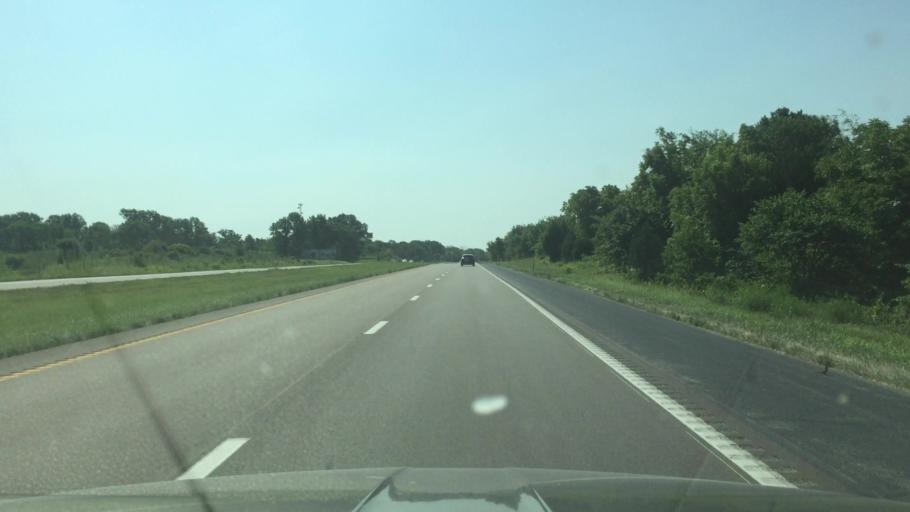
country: US
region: Missouri
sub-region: Pettis County
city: Sedalia
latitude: 38.7384
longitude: -93.3182
